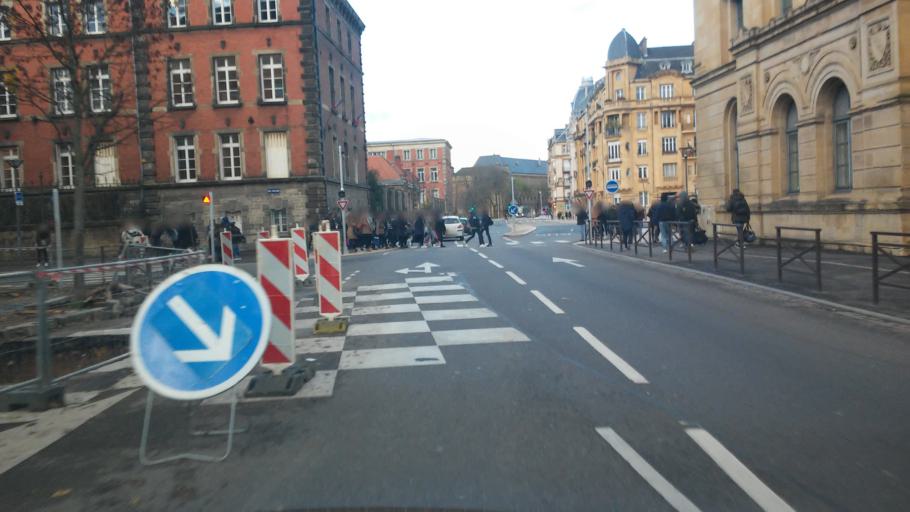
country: FR
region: Lorraine
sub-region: Departement de la Moselle
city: Metz
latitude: 49.1102
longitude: 6.1706
